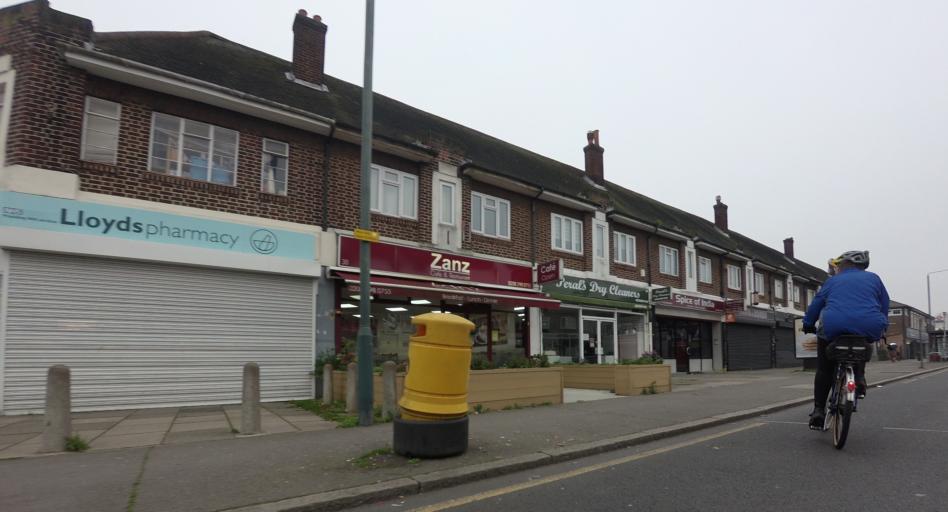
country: GB
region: England
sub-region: Greater London
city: Bexleyheath
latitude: 51.4649
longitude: 0.1330
